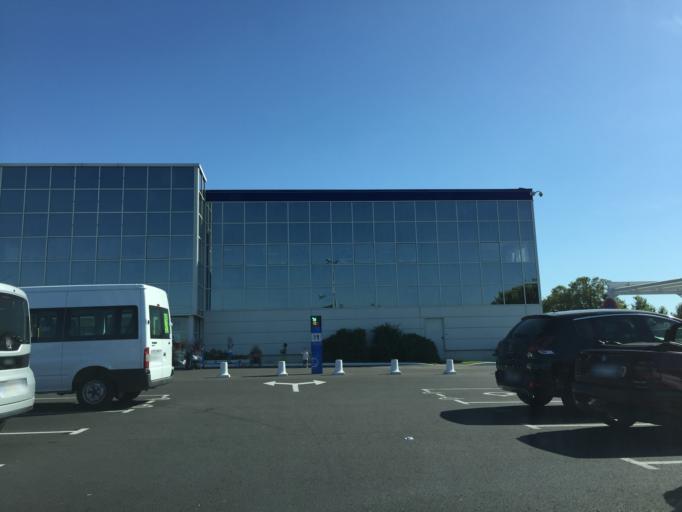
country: FR
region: Lower Normandy
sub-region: Departement du Calvados
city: Beuvillers
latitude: 49.1436
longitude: 0.2649
